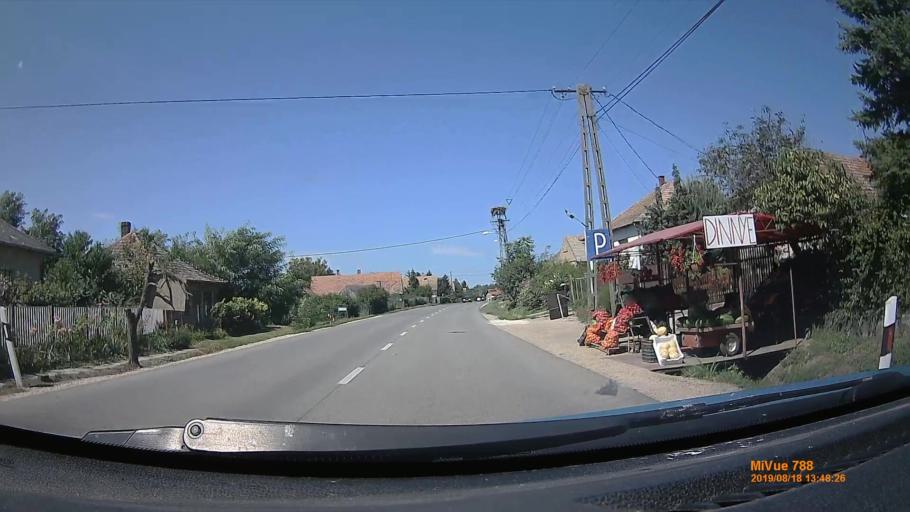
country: HU
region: Fejer
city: Cece
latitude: 46.7601
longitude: 18.6367
